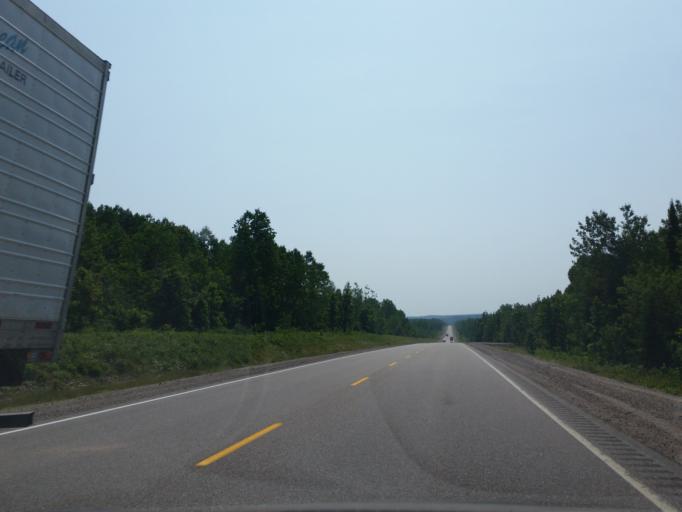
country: CA
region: Ontario
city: Mattawa
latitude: 46.2801
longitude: -78.3811
